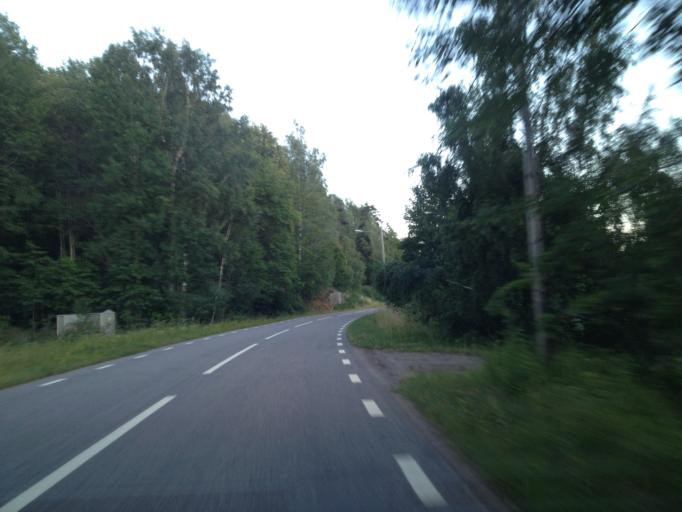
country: SE
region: Kalmar
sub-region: Vasterviks Kommun
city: Overum
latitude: 57.9922
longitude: 16.1867
